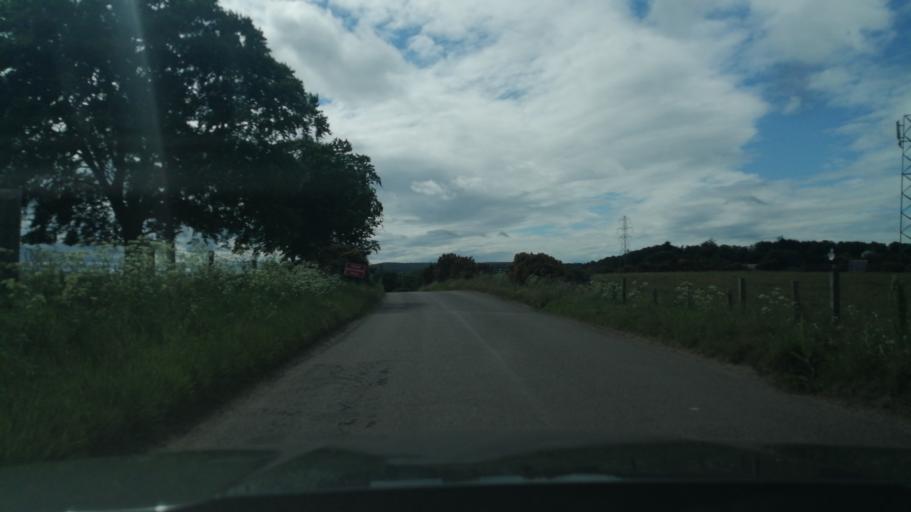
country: GB
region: Scotland
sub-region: Moray
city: Elgin
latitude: 57.6541
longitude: -3.2879
